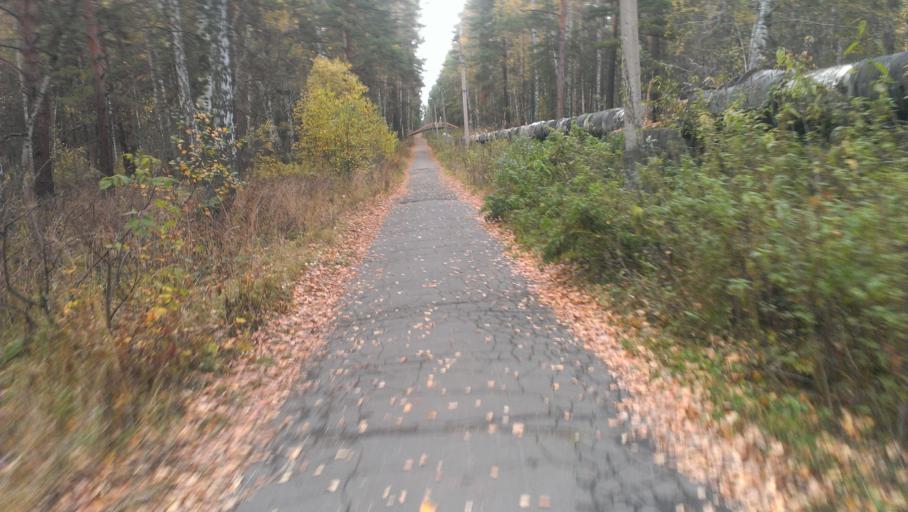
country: RU
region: Altai Krai
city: Yuzhnyy
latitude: 53.2631
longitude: 83.6864
